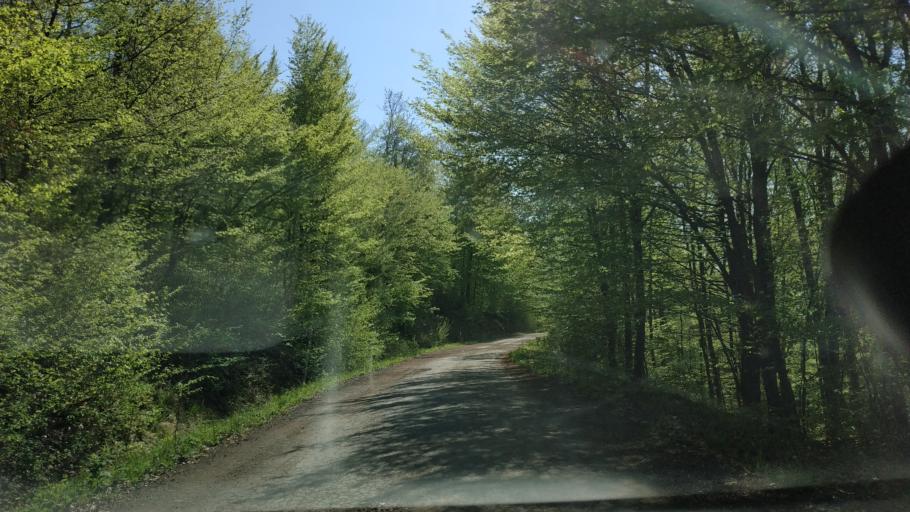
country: RS
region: Central Serbia
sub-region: Zajecarski Okrug
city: Soko Banja
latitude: 43.5067
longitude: 21.8978
